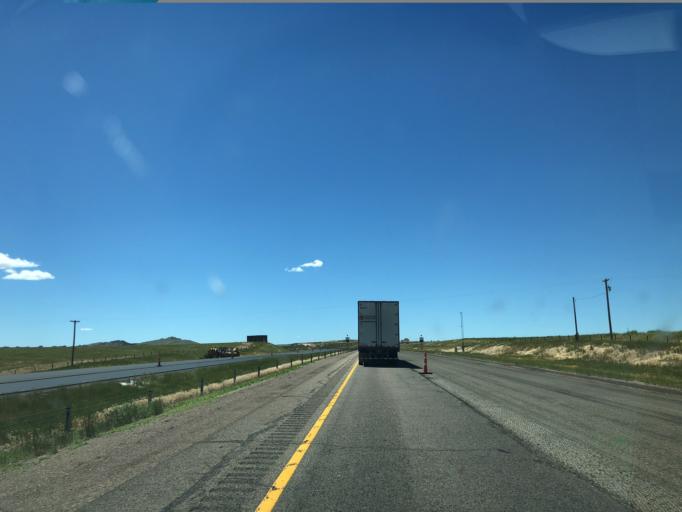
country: US
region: Wyoming
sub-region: Laramie County
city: Cheyenne
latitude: 41.0988
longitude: -105.1292
